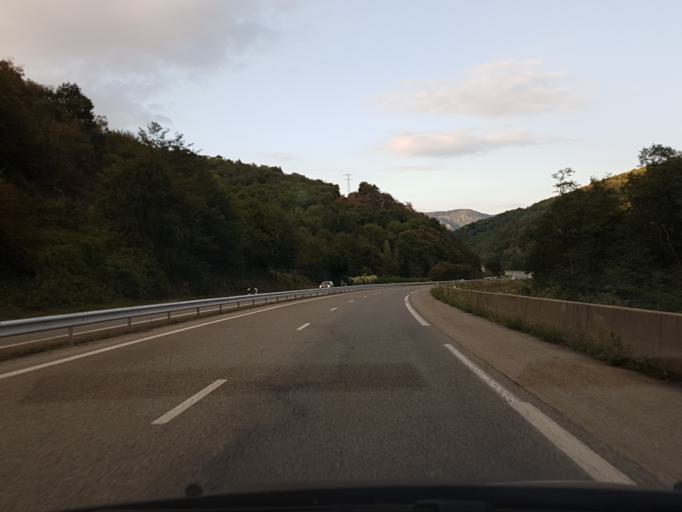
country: FR
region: Midi-Pyrenees
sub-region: Departement de l'Ariege
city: Mercus-Garrabet
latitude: 42.8984
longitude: 1.6325
